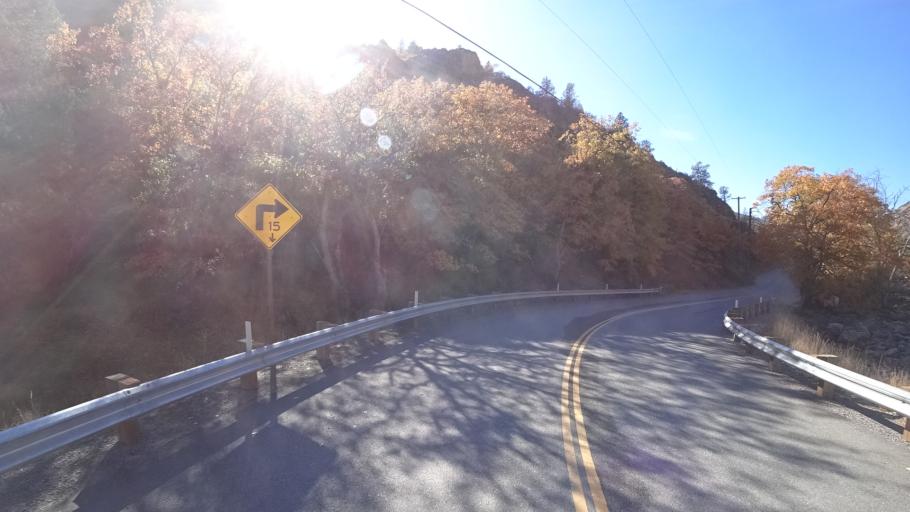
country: US
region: California
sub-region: Siskiyou County
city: Yreka
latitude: 41.8332
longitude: -122.6207
